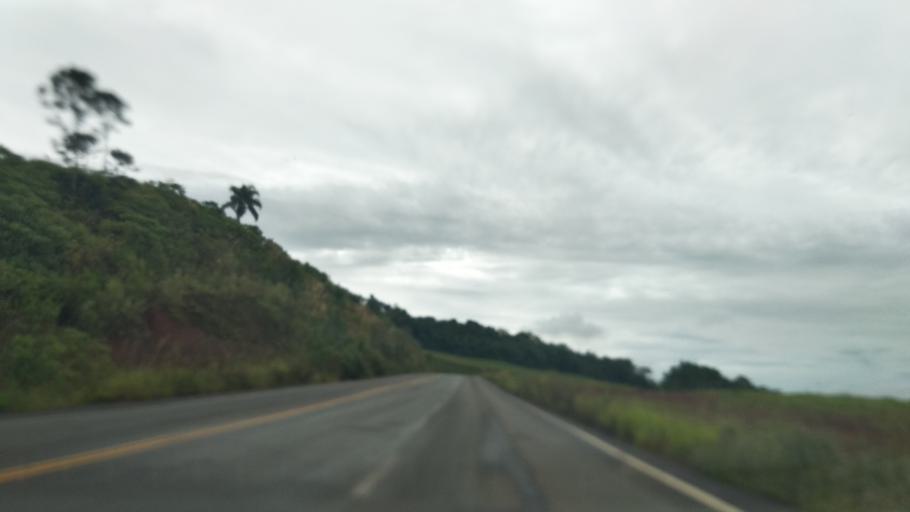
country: BR
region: Santa Catarina
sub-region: Videira
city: Videira
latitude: -27.0070
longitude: -51.1737
